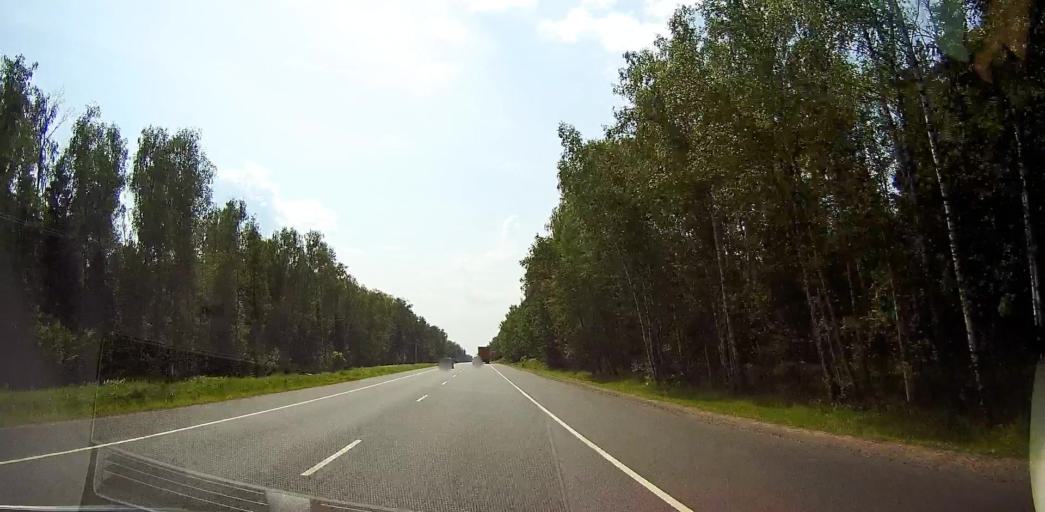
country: RU
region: Moskovskaya
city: Meshcherino
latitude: 55.2125
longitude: 38.3884
